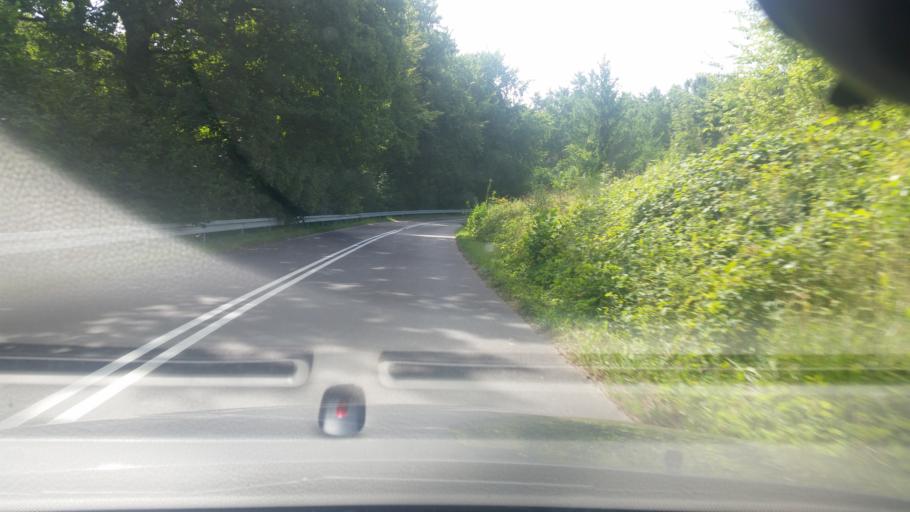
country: PL
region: Pomeranian Voivodeship
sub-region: Powiat wejherowski
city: Choczewo
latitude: 54.7573
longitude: 17.7515
